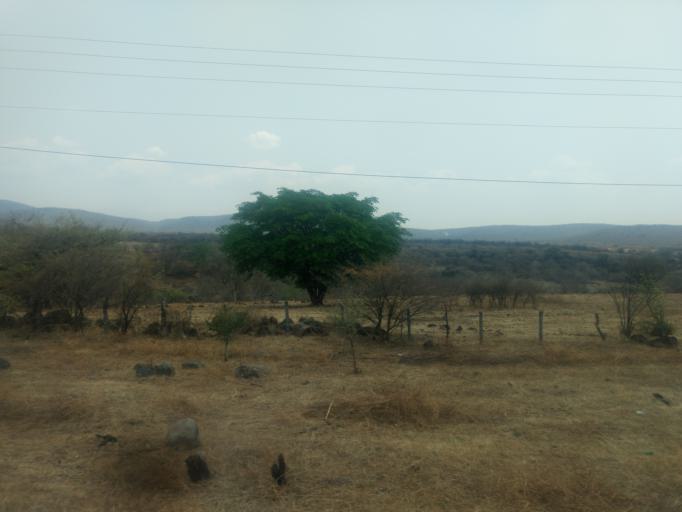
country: MX
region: Morelos
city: La Joya
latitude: 18.6702
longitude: -99.4298
